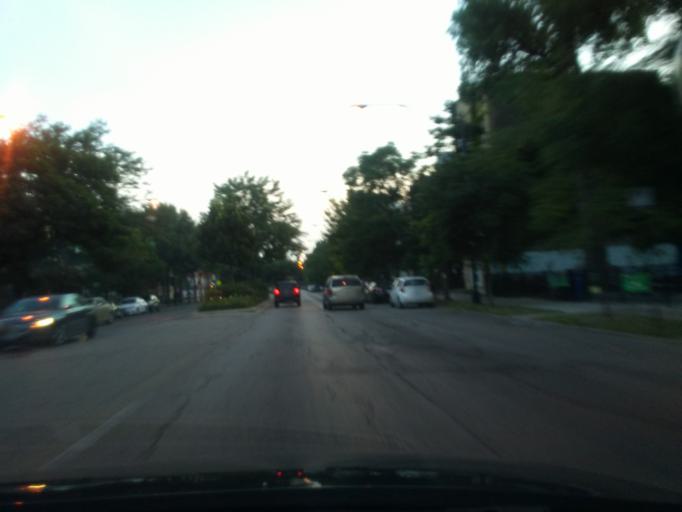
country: US
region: Illinois
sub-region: Cook County
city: Lincolnwood
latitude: 41.9770
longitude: -87.6696
